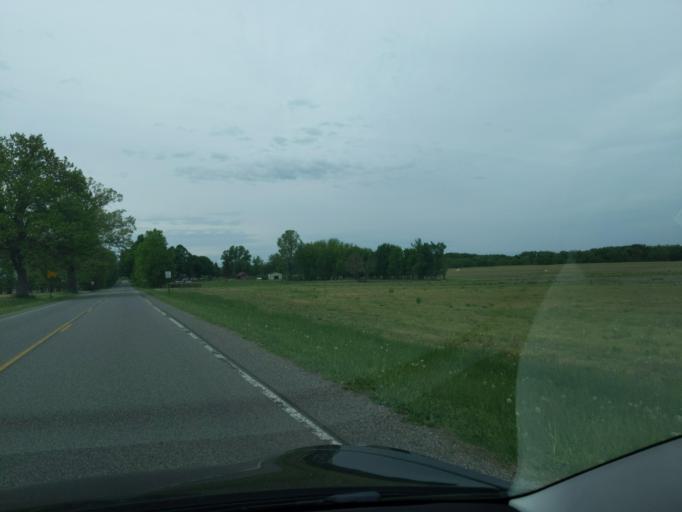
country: US
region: Michigan
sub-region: Ingham County
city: Leslie
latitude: 42.4746
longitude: -84.4236
